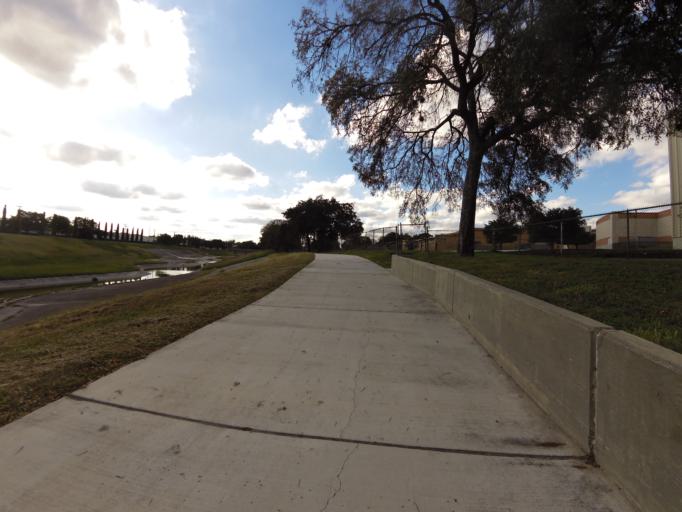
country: US
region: Texas
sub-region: Bexar County
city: San Antonio
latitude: 29.4141
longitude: -98.5248
